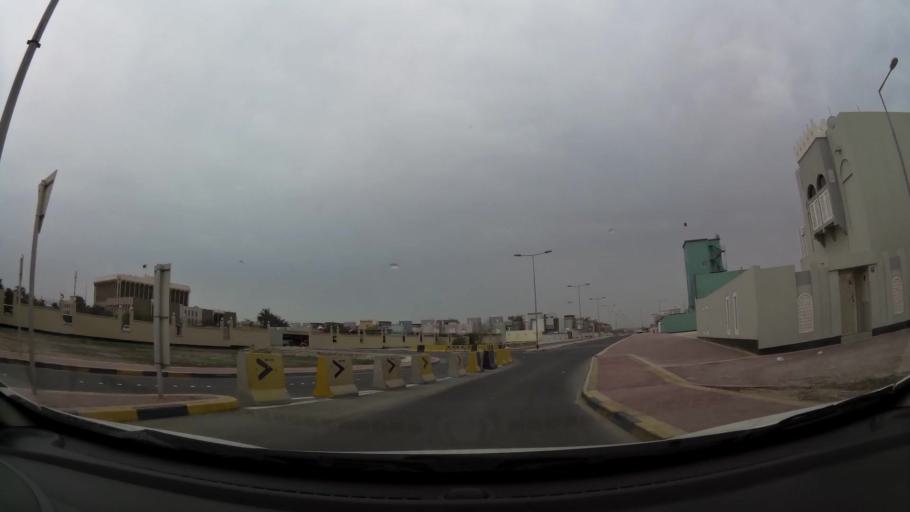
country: BH
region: Northern
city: Madinat `Isa
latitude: 26.1685
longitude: 50.5391
